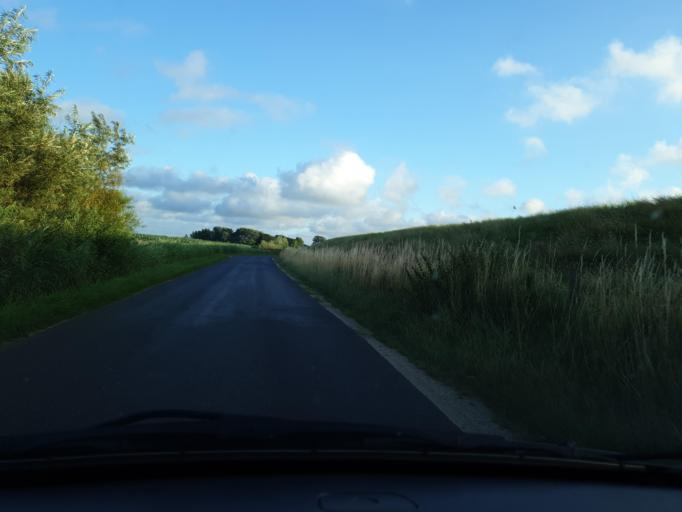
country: DE
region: Schleswig-Holstein
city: Elpersbuttel
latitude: 54.0882
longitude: 9.0315
